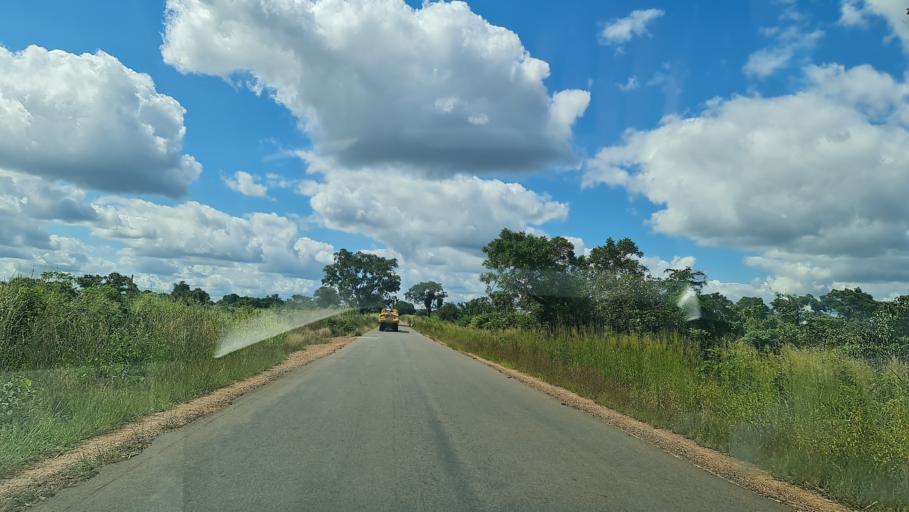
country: MZ
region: Zambezia
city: Quelimane
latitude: -17.5131
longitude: 36.2250
